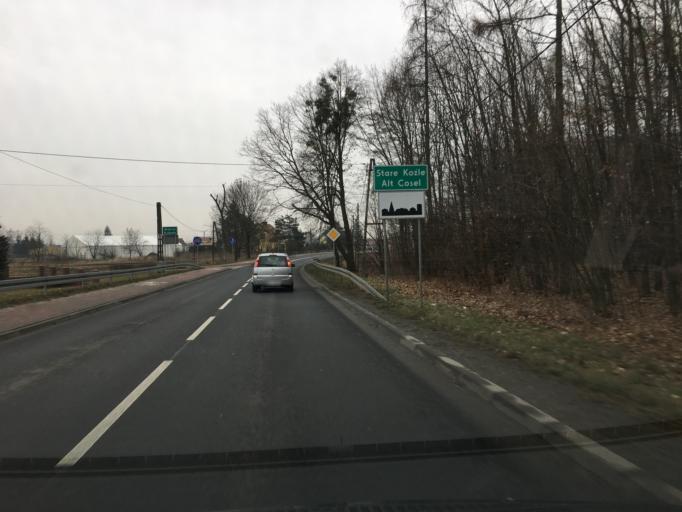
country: PL
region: Opole Voivodeship
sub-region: Powiat kedzierzynsko-kozielski
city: Kedzierzyn-Kozle
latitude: 50.3186
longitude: 18.2232
